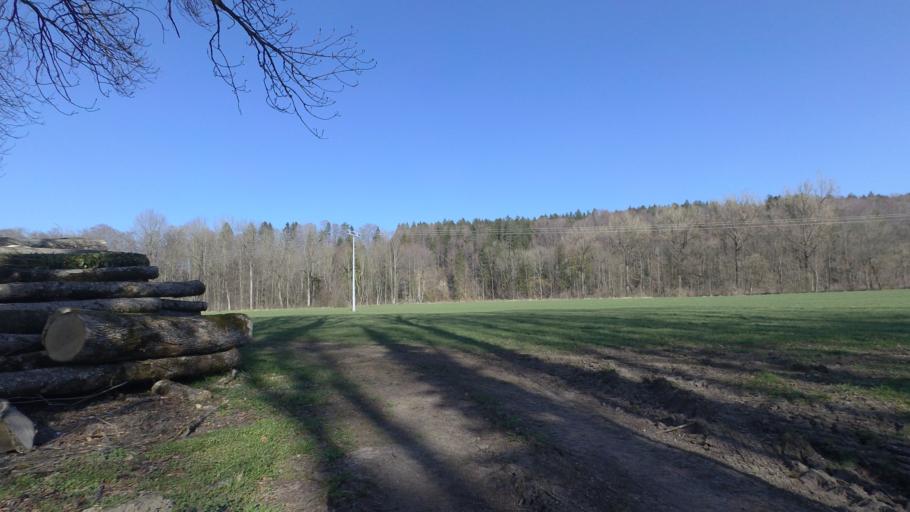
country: DE
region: Bavaria
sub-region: Upper Bavaria
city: Nussdorf
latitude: 47.9217
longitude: 12.6225
